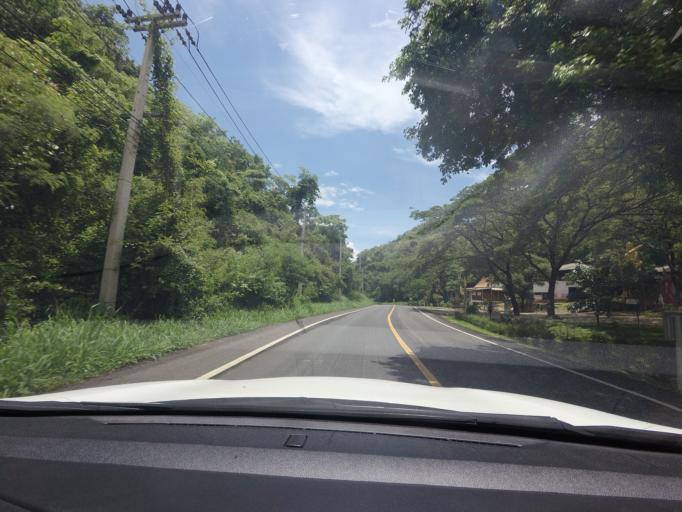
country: TH
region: Sara Buri
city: Muak Lek
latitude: 14.5748
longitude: 101.2774
